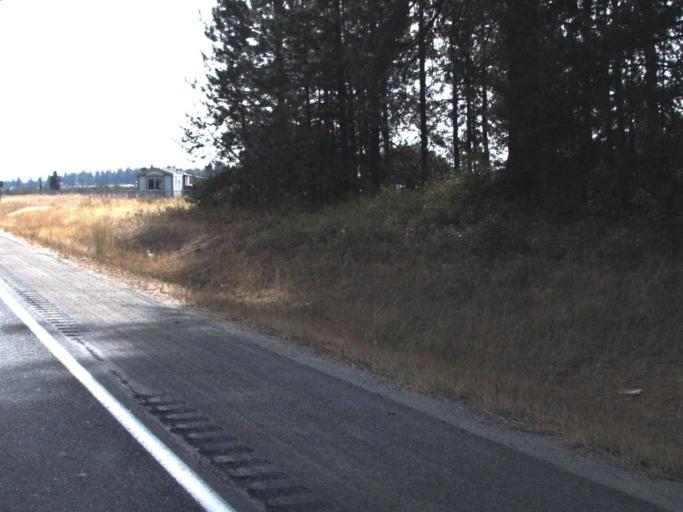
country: US
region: Washington
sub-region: Spokane County
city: Deer Park
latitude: 47.9994
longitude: -117.5740
